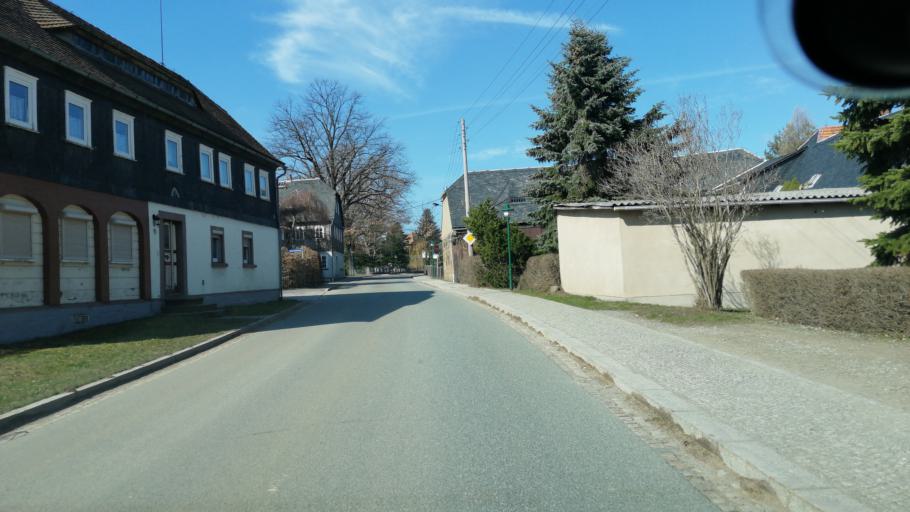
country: DE
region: Saxony
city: Schonbach
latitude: 51.0618
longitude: 14.5683
